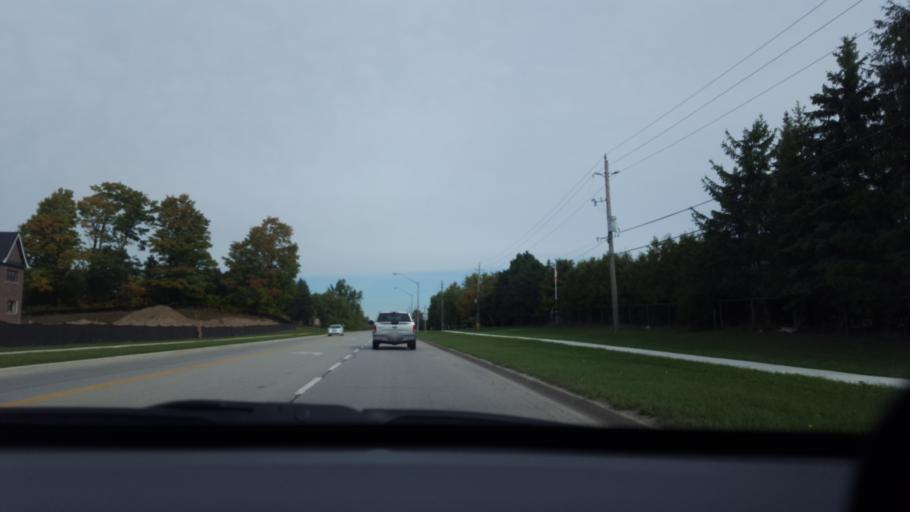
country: CA
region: Ontario
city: Vaughan
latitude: 43.9383
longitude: -79.5307
